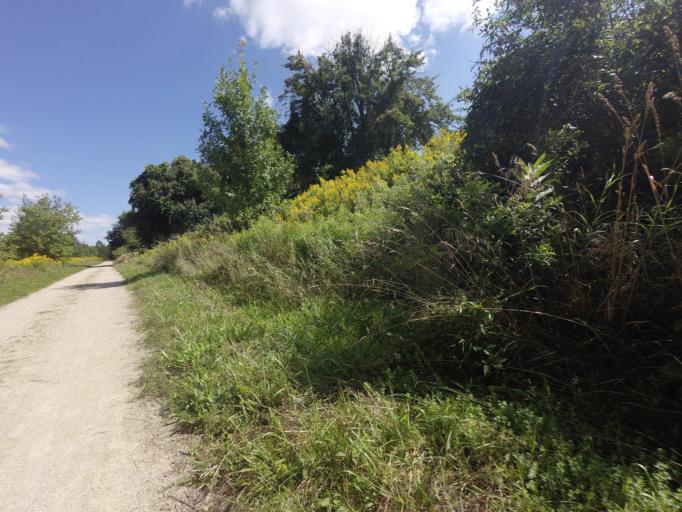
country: CA
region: Ontario
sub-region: Wellington County
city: Guelph
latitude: 43.7881
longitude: -80.3180
